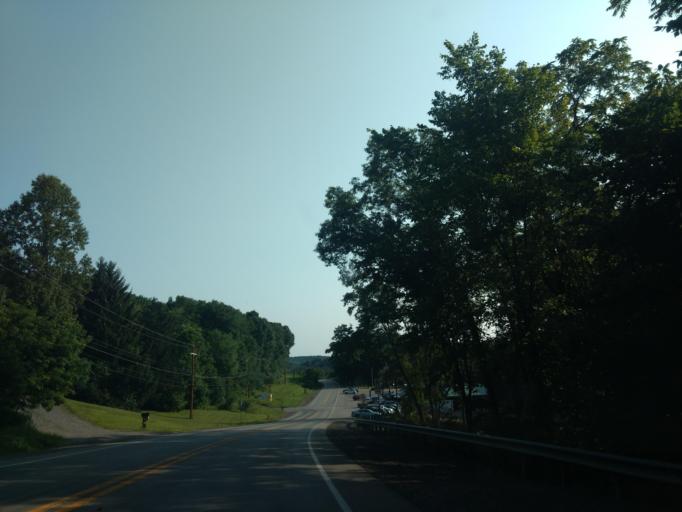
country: US
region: Pennsylvania
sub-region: Butler County
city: Zelienople
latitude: 40.8349
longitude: -80.1197
